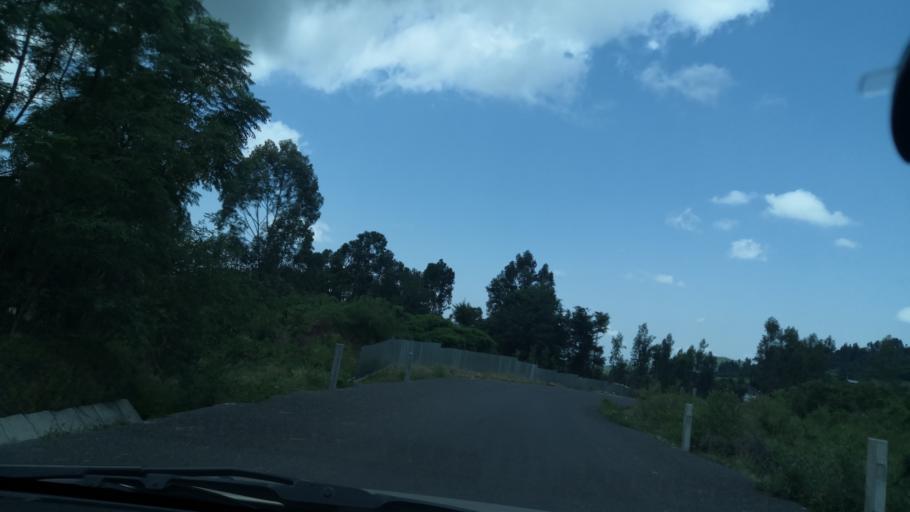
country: ET
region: Amhara
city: Abomsa
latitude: 10.3182
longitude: 39.8741
